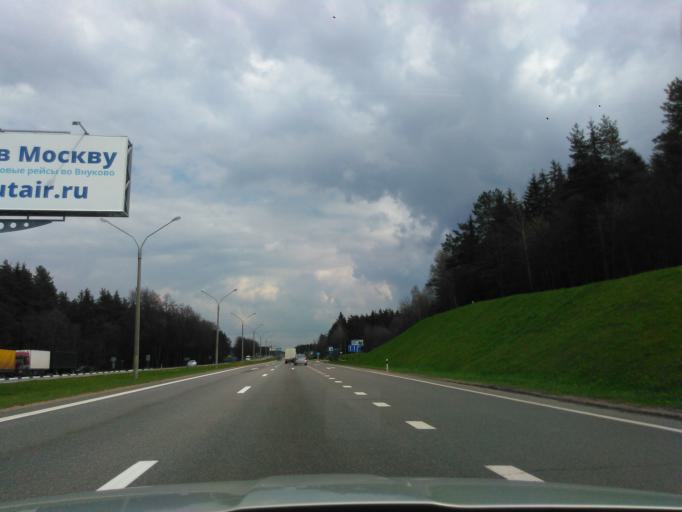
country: BY
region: Minsk
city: Korolev Stan
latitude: 53.9929
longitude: 27.8106
